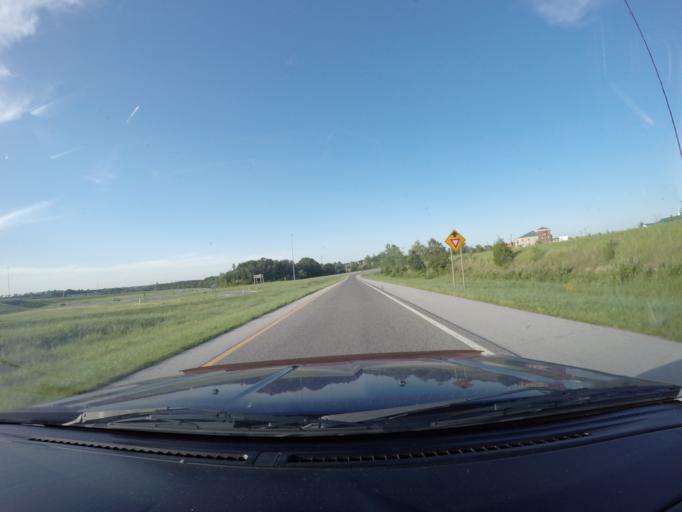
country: US
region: Kansas
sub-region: Wyandotte County
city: Edwardsville
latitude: 39.1410
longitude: -94.8180
